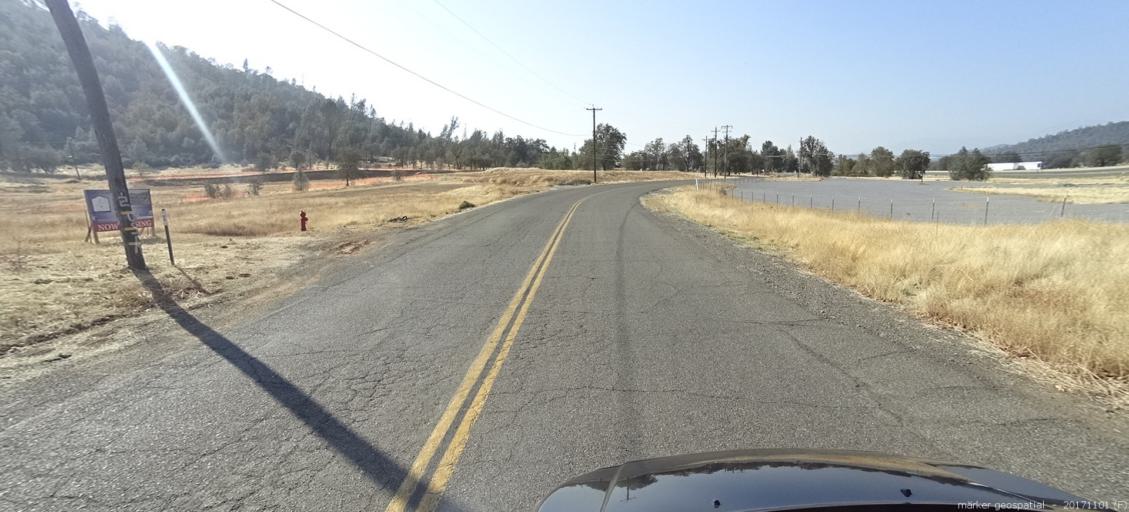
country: US
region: California
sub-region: Shasta County
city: Shasta Lake
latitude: 40.7050
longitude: -122.3353
